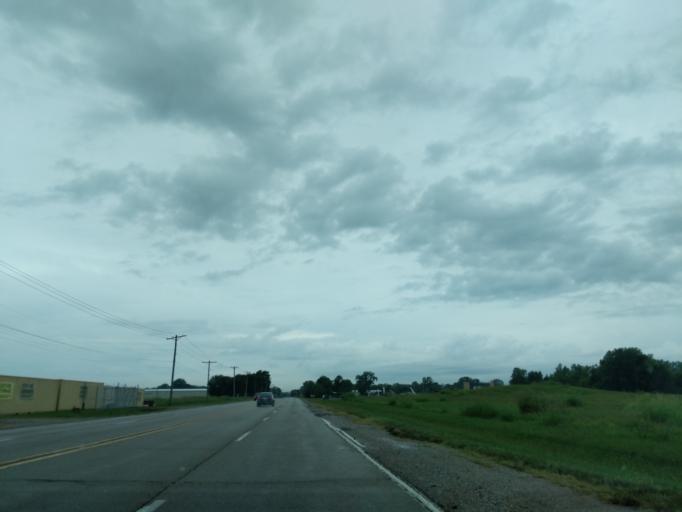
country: US
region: Illinois
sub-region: Saint Clair County
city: Fairmont City
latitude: 38.6590
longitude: -90.0716
